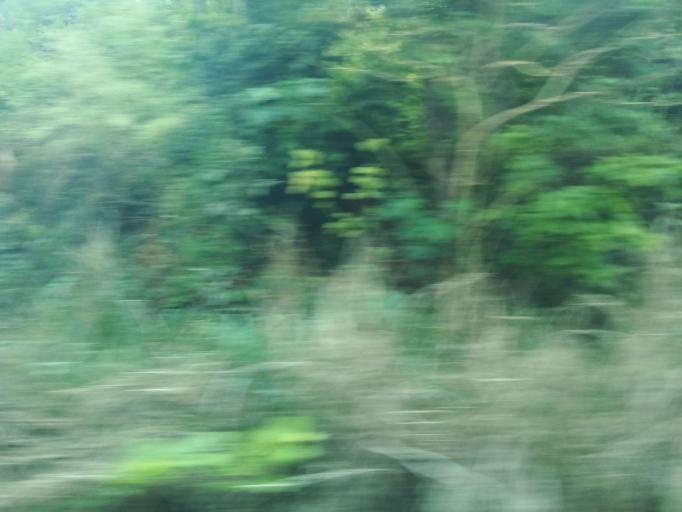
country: BR
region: Minas Gerais
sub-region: Ipaba
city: Ipaba
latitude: -19.4619
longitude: -42.4485
